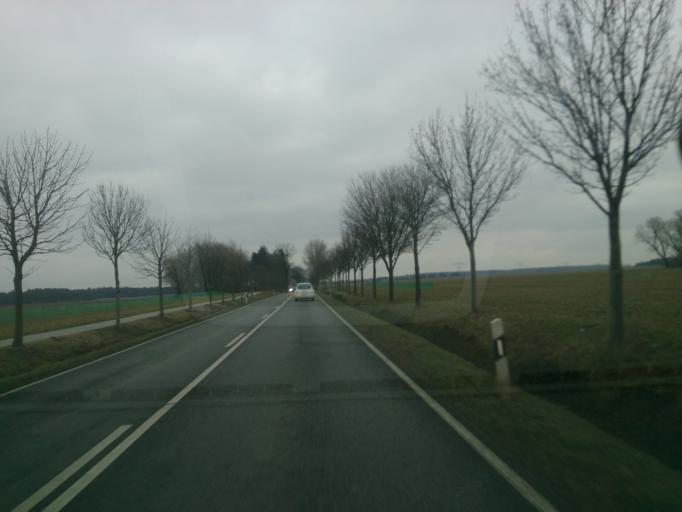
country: DE
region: Mecklenburg-Vorpommern
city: Demmin
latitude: 53.8758
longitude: 13.0205
